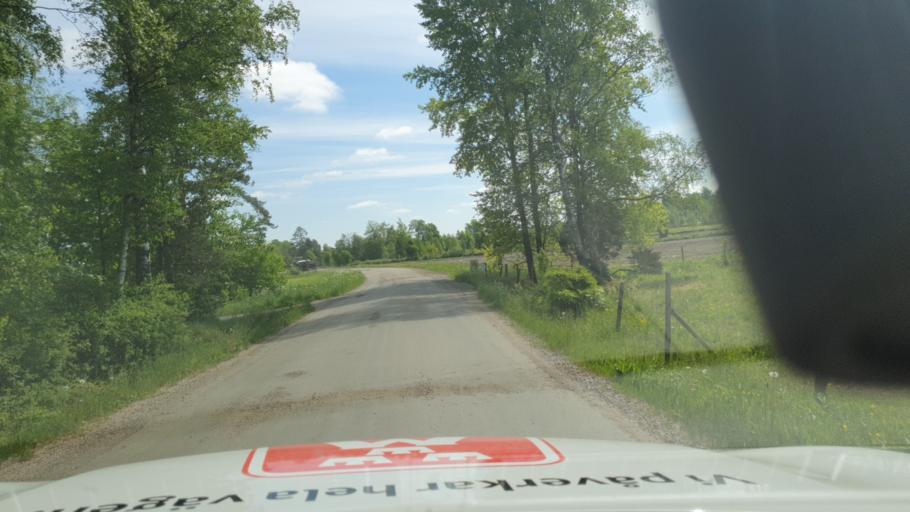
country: SE
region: Vaestra Goetaland
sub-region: Herrljunga Kommun
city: Herrljunga
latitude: 57.9477
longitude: 12.9946
